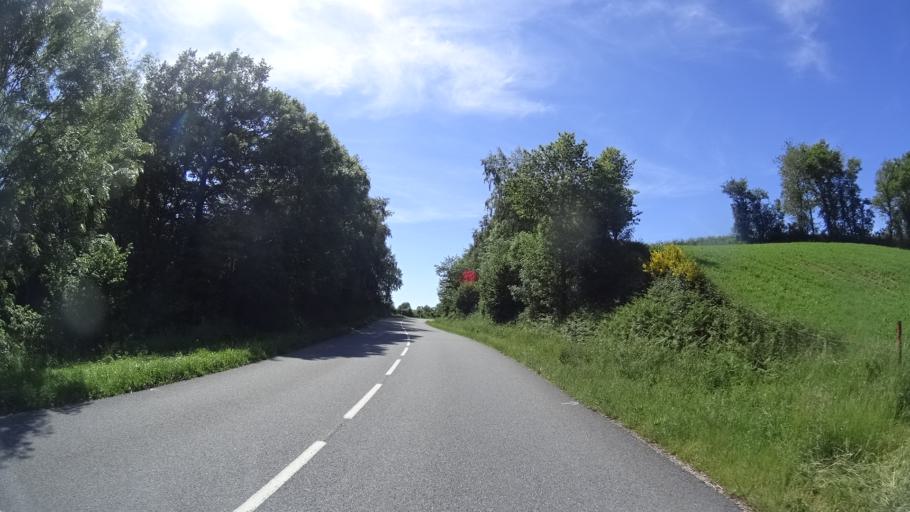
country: FR
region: Midi-Pyrenees
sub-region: Departement de l'Aveyron
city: Pont-de-Salars
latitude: 44.3318
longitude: 2.7718
